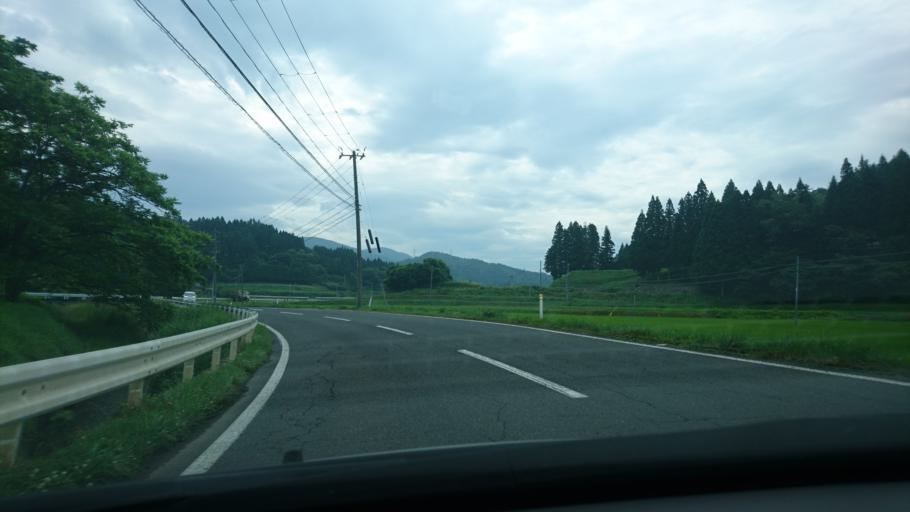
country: JP
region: Iwate
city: Ichinoseki
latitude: 38.9067
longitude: 141.4224
